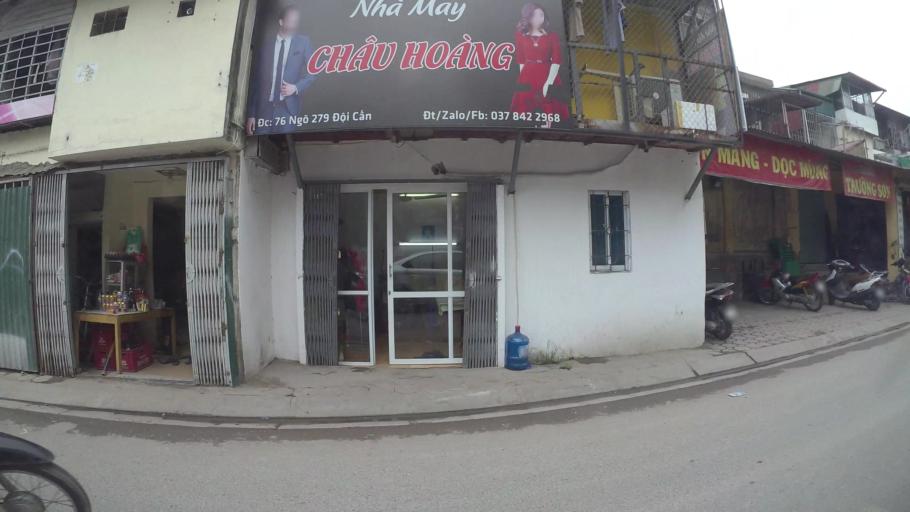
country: VN
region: Ha Noi
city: Dong Da
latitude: 21.0387
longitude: 105.8221
